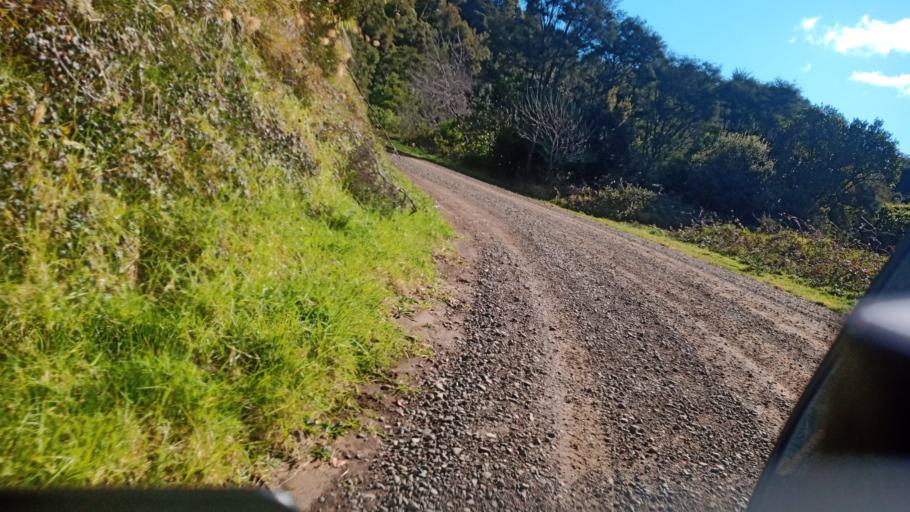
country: NZ
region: Bay of Plenty
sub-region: Opotiki District
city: Opotiki
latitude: -38.0397
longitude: 177.4438
